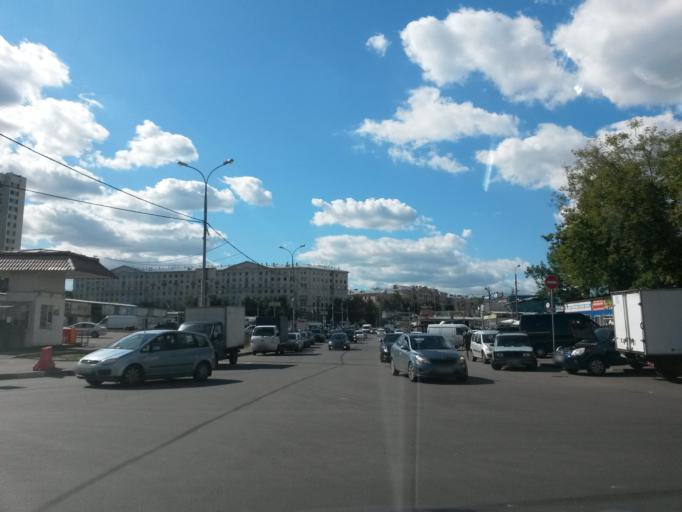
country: RU
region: Moskovskaya
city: Kozhukhovo
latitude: 55.7046
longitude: 37.6904
